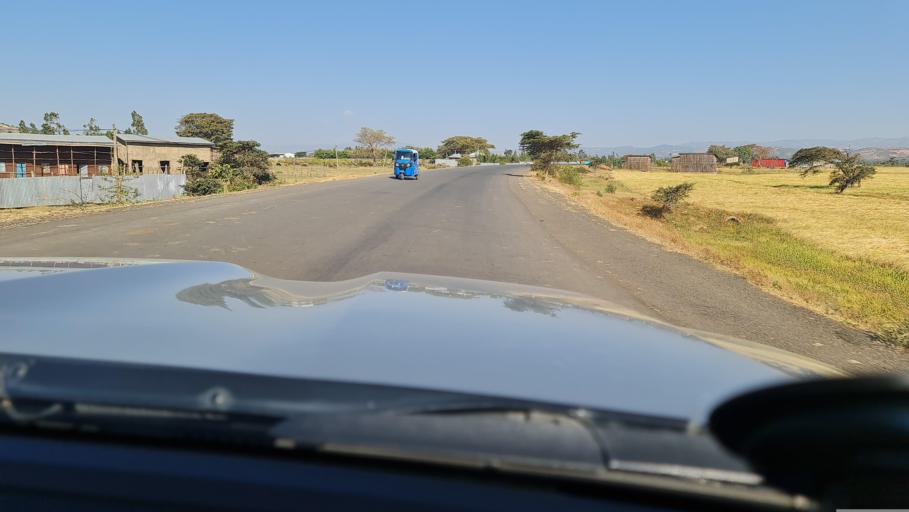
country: ET
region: Oromiya
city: Waliso
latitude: 8.5544
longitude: 37.9510
